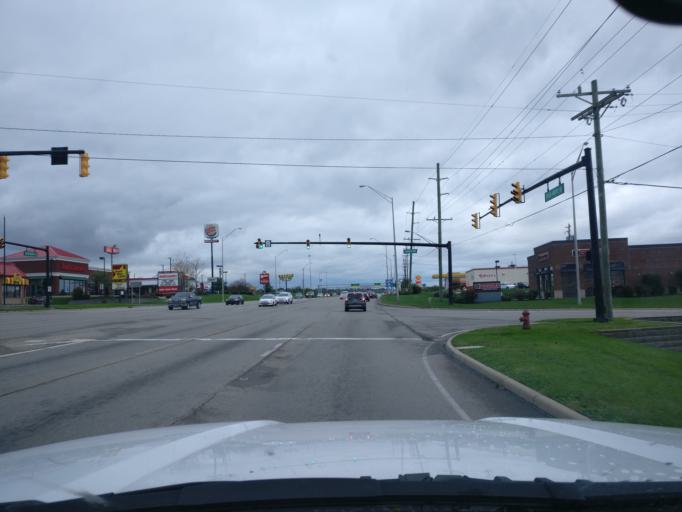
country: US
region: Ohio
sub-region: Butler County
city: Monroe
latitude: 39.4397
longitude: -84.3299
